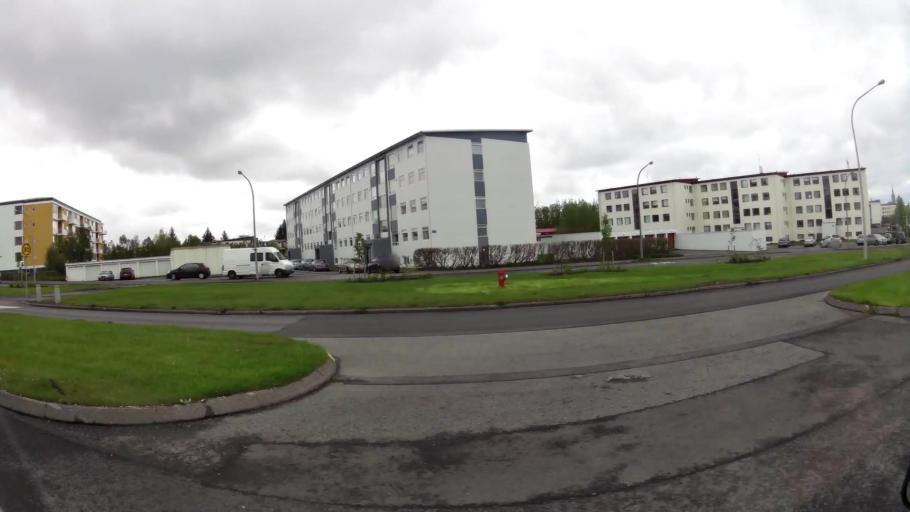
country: IS
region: Capital Region
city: Reykjavik
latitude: 64.1368
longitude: -21.8874
